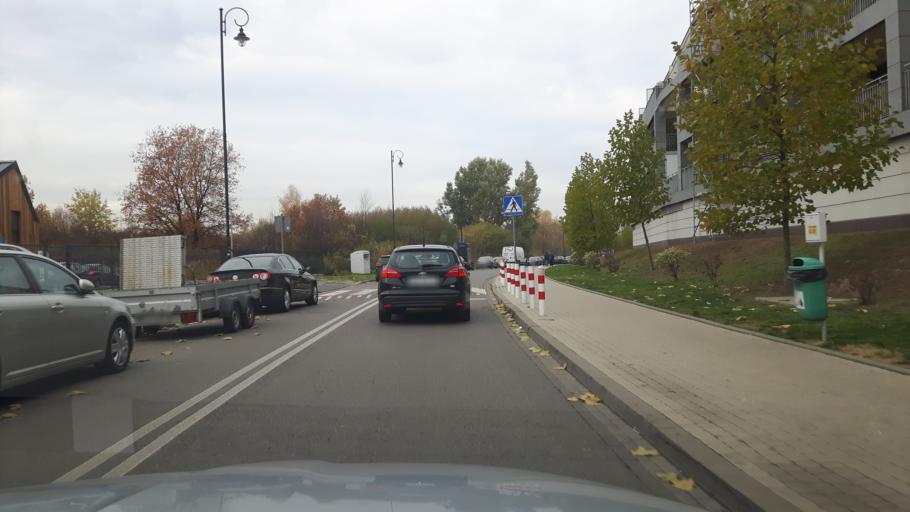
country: PL
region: Masovian Voivodeship
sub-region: Warszawa
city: Ursynow
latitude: 52.1599
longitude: 21.0648
